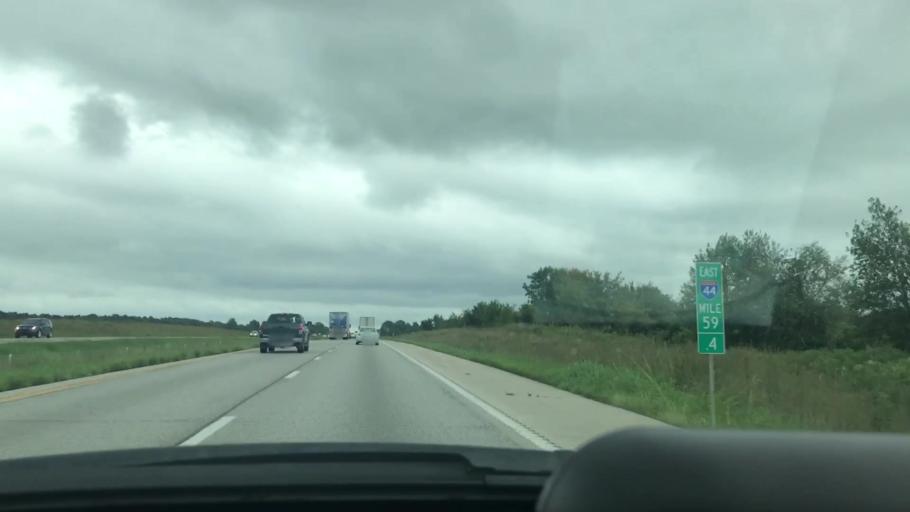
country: US
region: Missouri
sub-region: Greene County
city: Ash Grove
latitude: 37.1862
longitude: -93.6147
